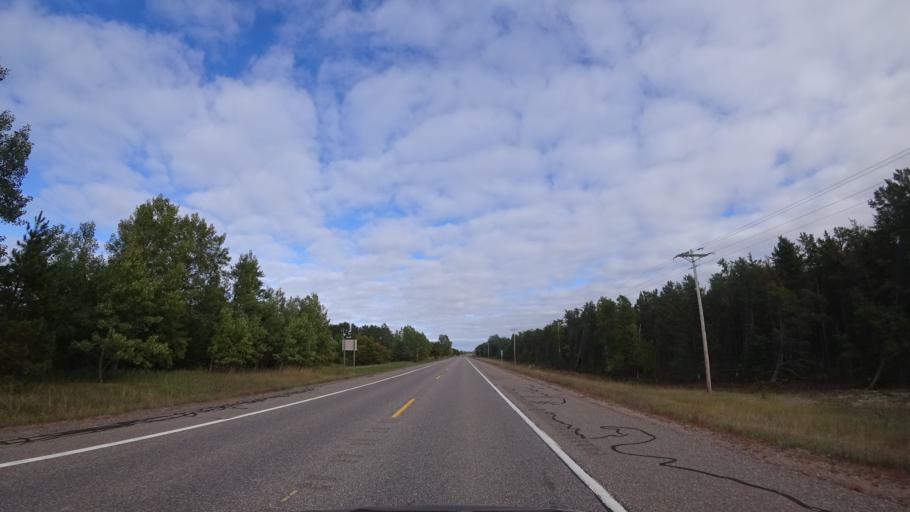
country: US
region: Michigan
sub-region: Marquette County
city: Harvey
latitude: 46.4899
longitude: -87.2044
